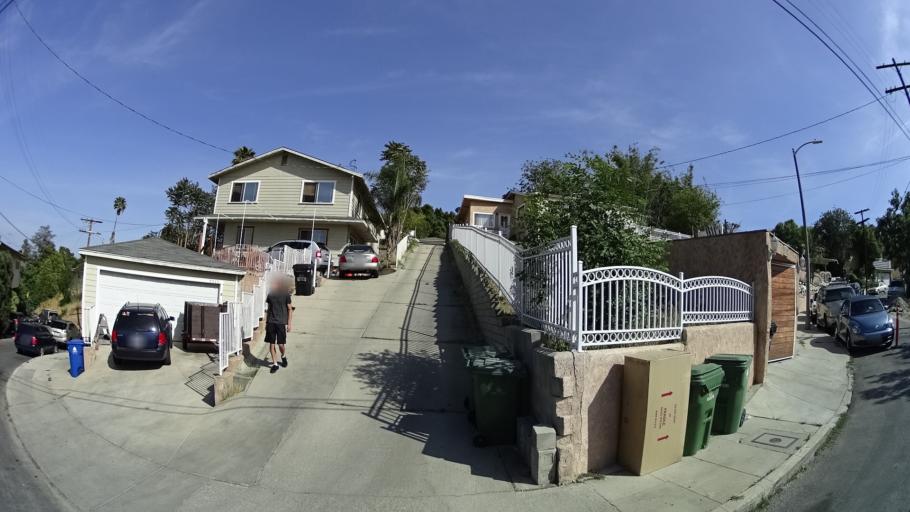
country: US
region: California
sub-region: Los Angeles County
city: Belvedere
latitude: 34.0750
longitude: -118.1763
